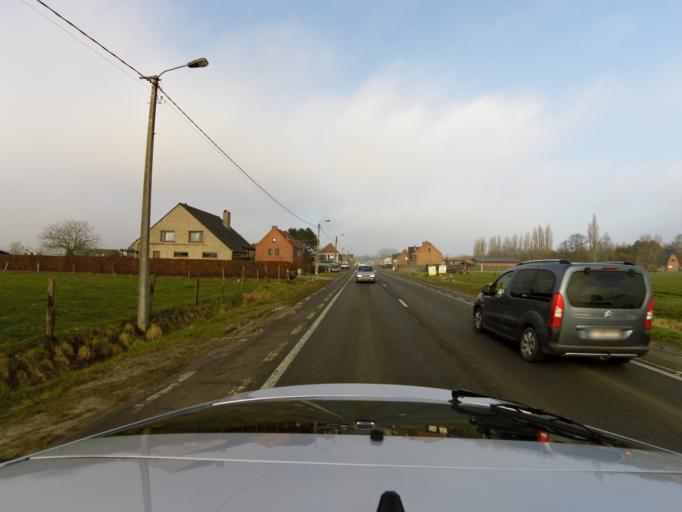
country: BE
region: Flanders
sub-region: Provincie West-Vlaanderen
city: Torhout
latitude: 51.0737
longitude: 3.0757
